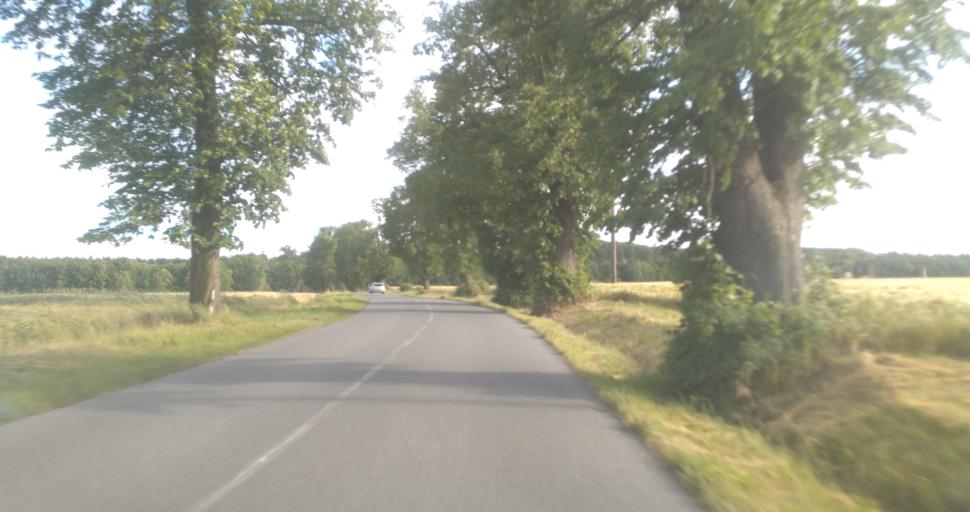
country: CZ
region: Central Bohemia
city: Roztoky
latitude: 49.9755
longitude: 13.8991
